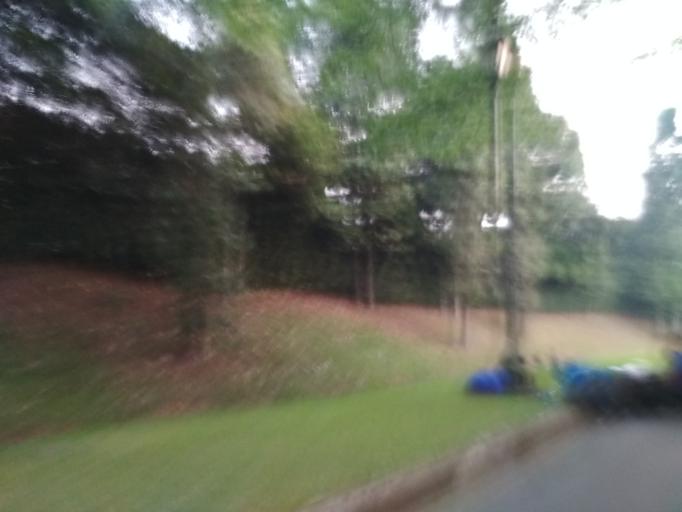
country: ID
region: West Java
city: Caringin
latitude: -6.6627
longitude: 106.8425
